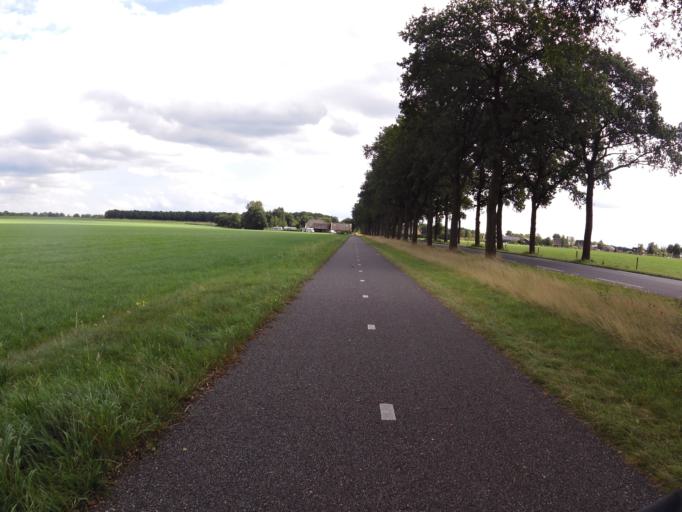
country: NL
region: Drenthe
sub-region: Gemeente Borger-Odoorn
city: Borger
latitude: 52.9277
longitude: 6.7713
